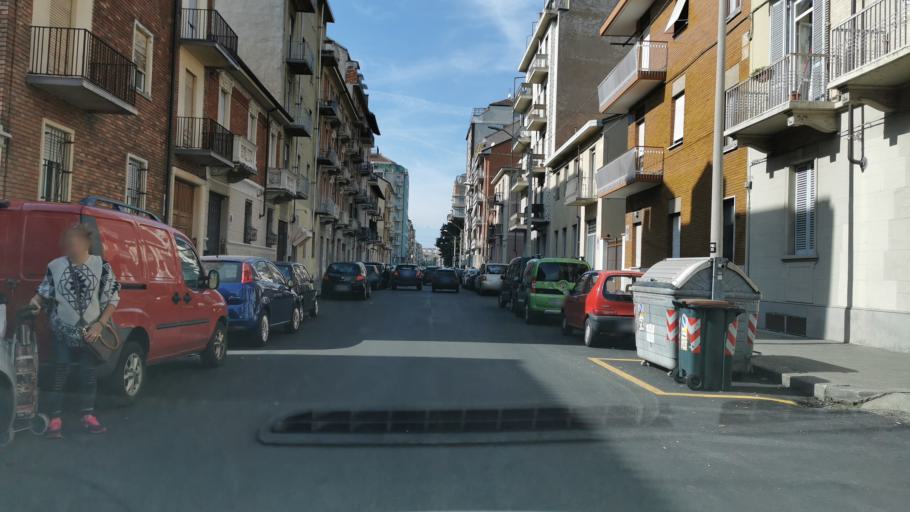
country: IT
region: Piedmont
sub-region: Provincia di Torino
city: Turin
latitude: 45.0989
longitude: 7.6649
